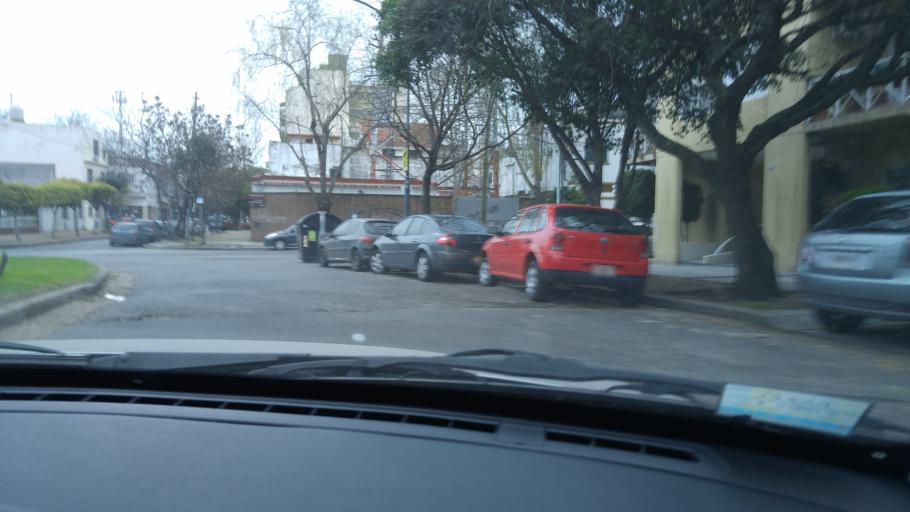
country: AR
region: Buenos Aires F.D.
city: Villa Santa Rita
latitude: -34.6284
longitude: -58.5244
